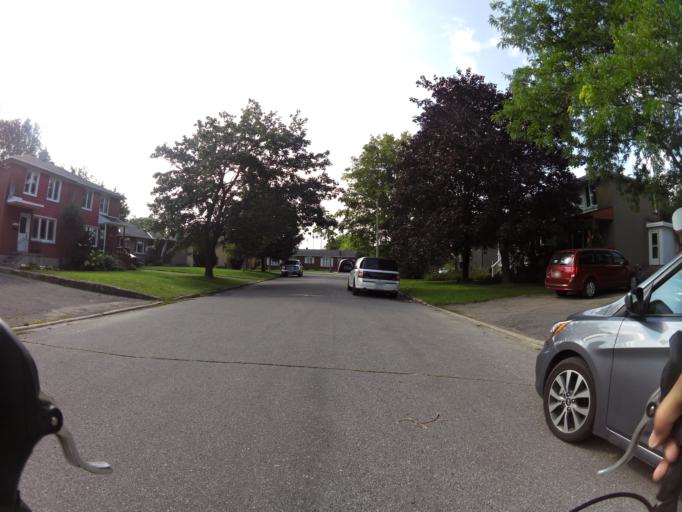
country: CA
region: Ontario
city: Ottawa
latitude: 45.3748
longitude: -75.6741
